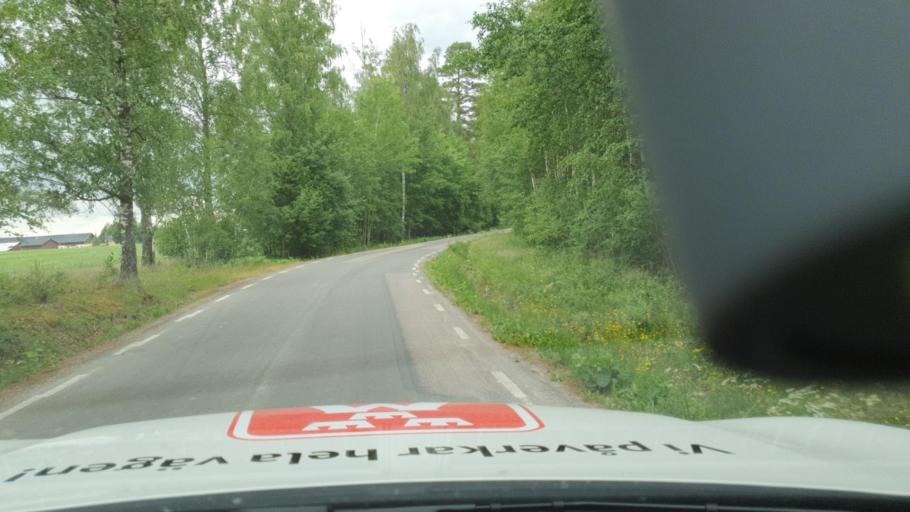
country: SE
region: Vaestra Goetaland
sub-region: Tidaholms Kommun
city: Olofstorp
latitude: 58.2840
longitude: 14.1028
